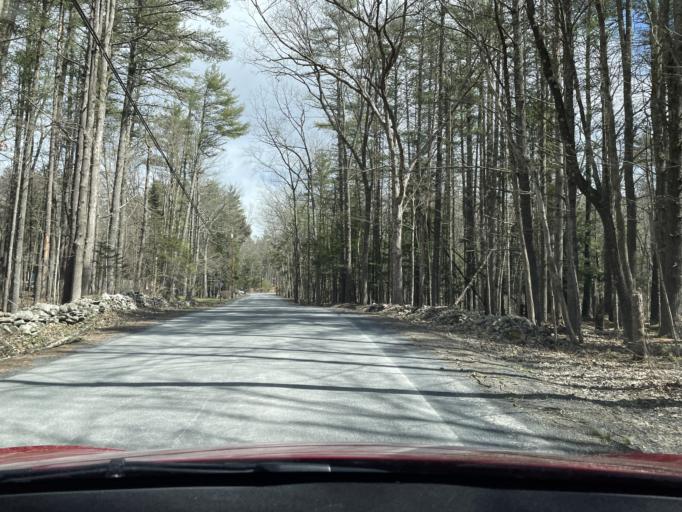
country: US
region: New York
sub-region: Ulster County
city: Zena
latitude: 42.0182
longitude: -74.0651
